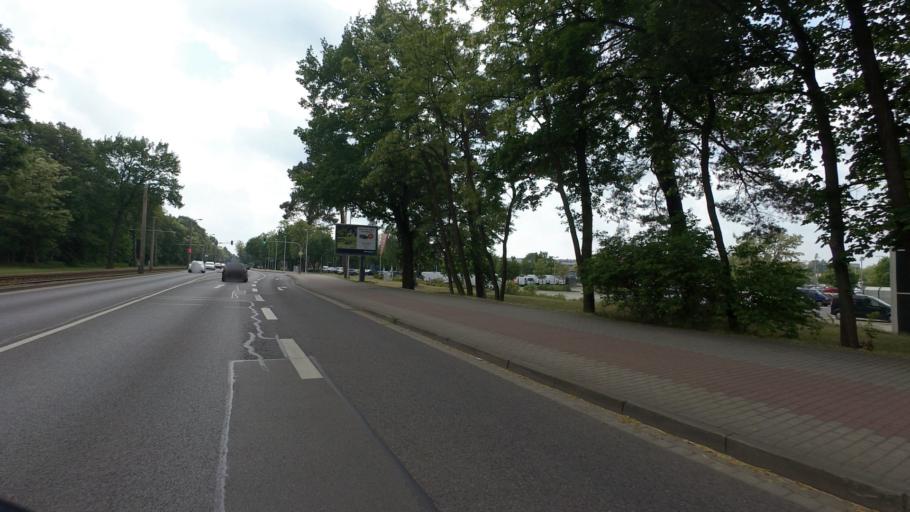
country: DE
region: Brandenburg
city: Cottbus
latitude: 51.7354
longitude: 14.3371
